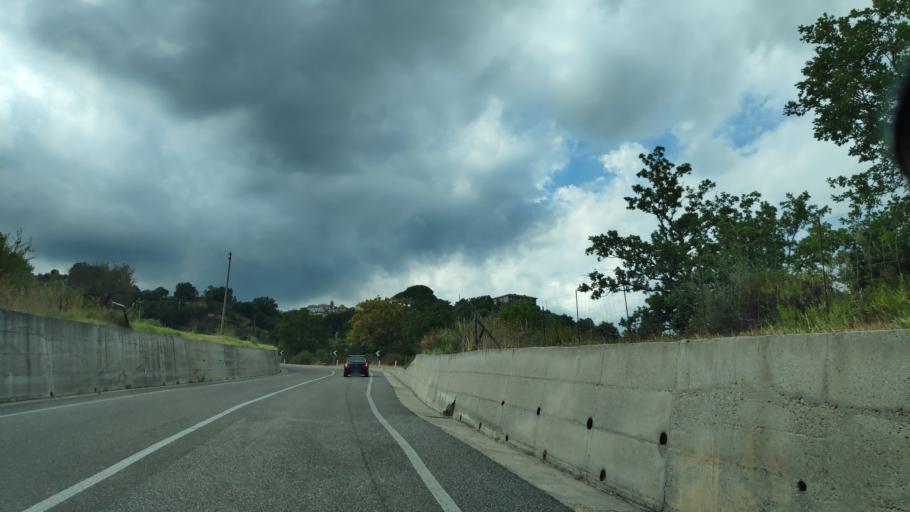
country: IT
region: Calabria
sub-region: Provincia di Catanzaro
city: Santa Caterina dello Ionio
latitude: 38.5283
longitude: 16.5283
